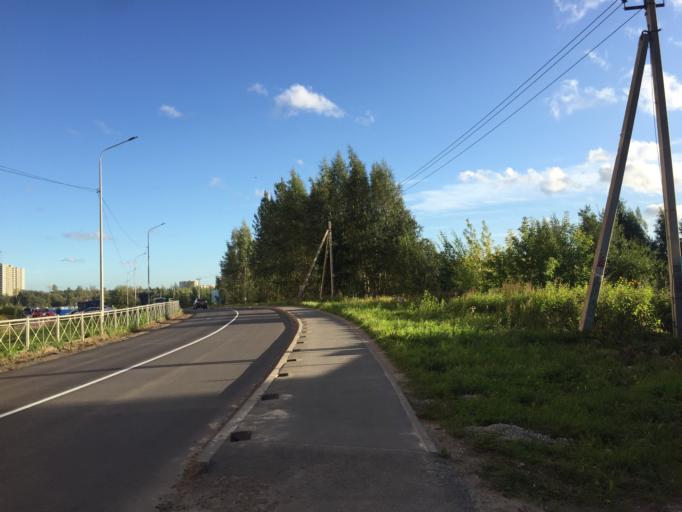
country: RU
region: Leningrad
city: Murino
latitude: 60.0594
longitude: 30.4575
